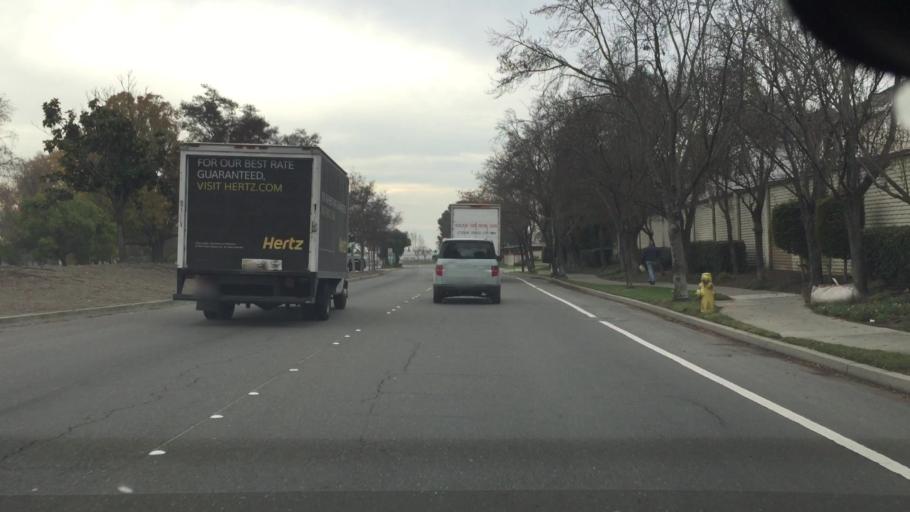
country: US
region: California
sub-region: Alameda County
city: Fremont
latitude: 37.5162
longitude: -121.9931
